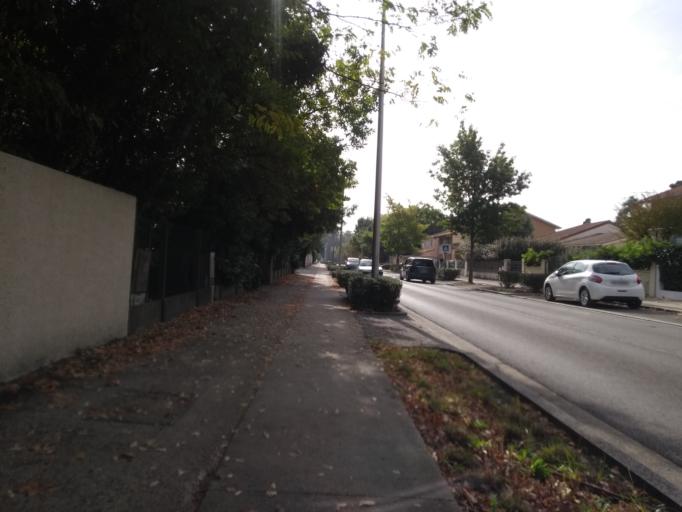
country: FR
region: Aquitaine
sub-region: Departement de la Gironde
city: Pessac
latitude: 44.7974
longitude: -0.6307
